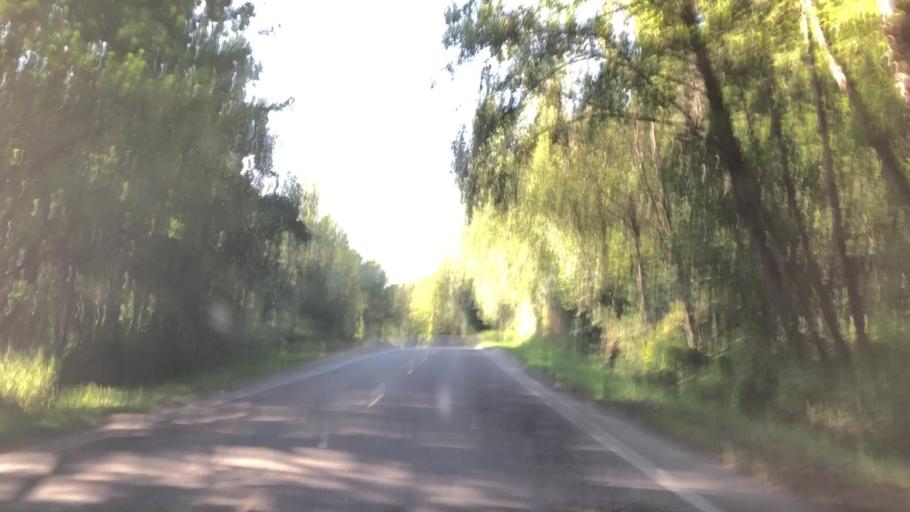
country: US
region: Washington
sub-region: King County
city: Woodinville
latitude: 47.7671
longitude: -122.1754
